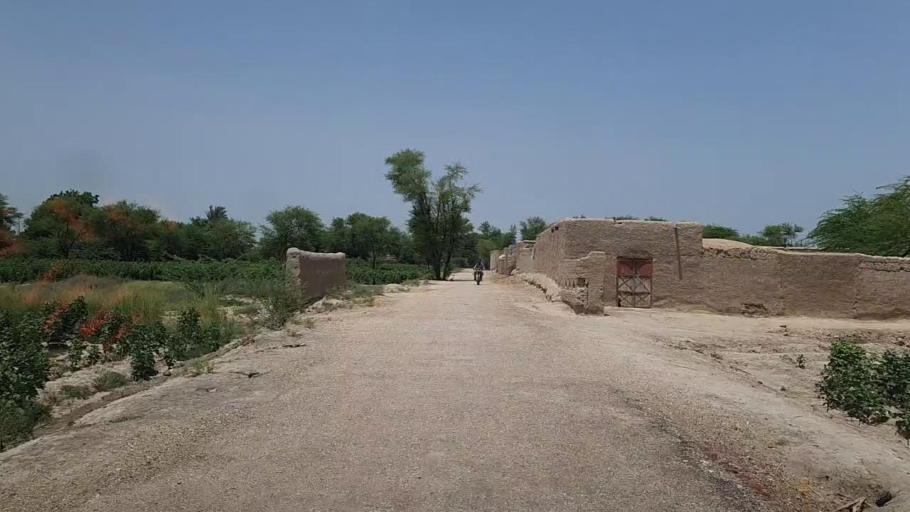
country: PK
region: Sindh
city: Pad Idan
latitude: 26.7536
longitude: 68.3107
